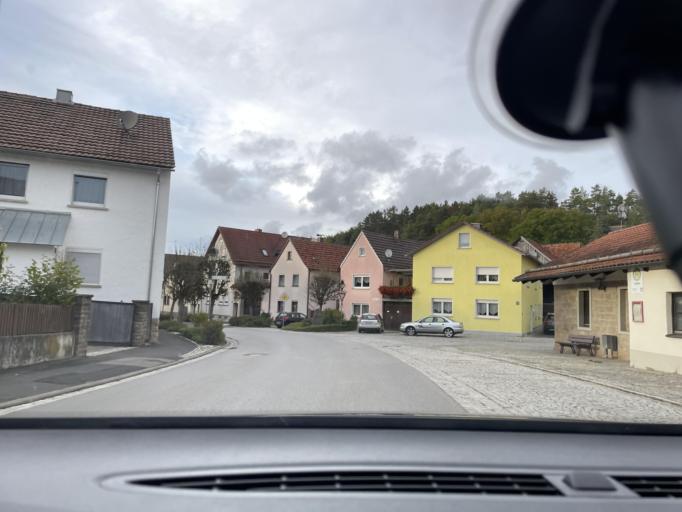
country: DE
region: Bavaria
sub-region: Regierungsbezirk Unterfranken
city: Strahlungen
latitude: 50.2990
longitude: 10.2491
